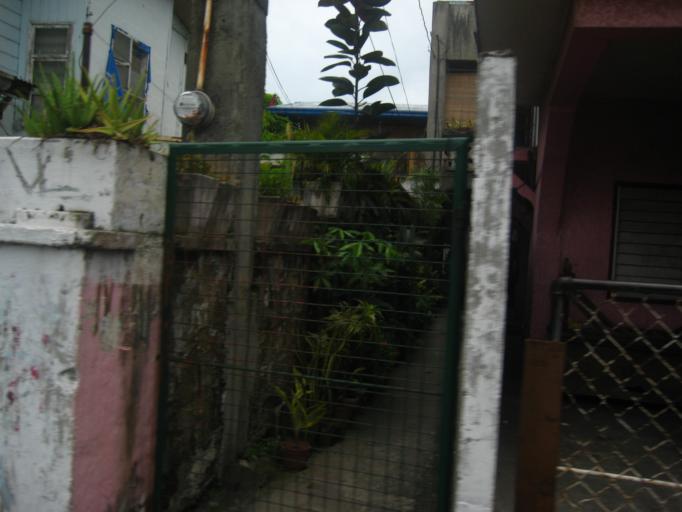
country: PH
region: Calabarzon
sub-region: Province of Rizal
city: Pateros
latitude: 14.5408
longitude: 121.0698
